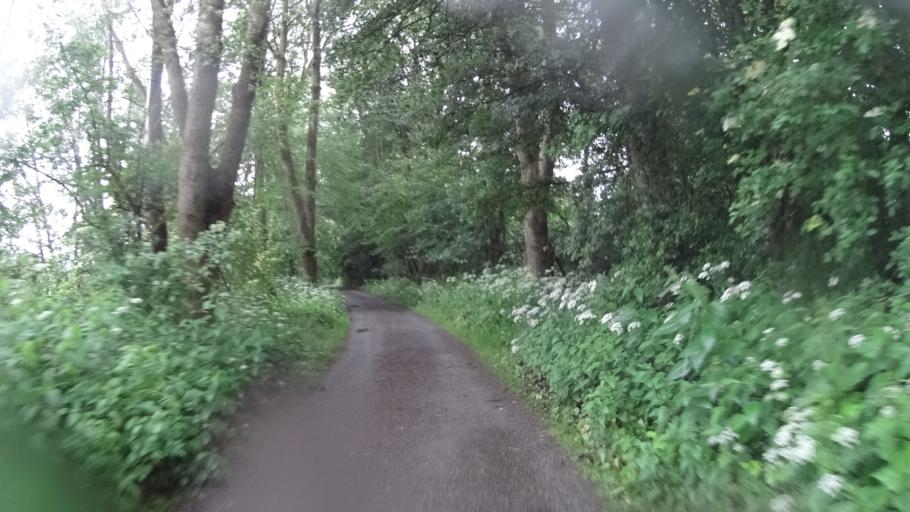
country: AT
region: Upper Austria
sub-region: Politischer Bezirk Scharding
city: Scharding
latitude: 48.4717
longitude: 13.4290
